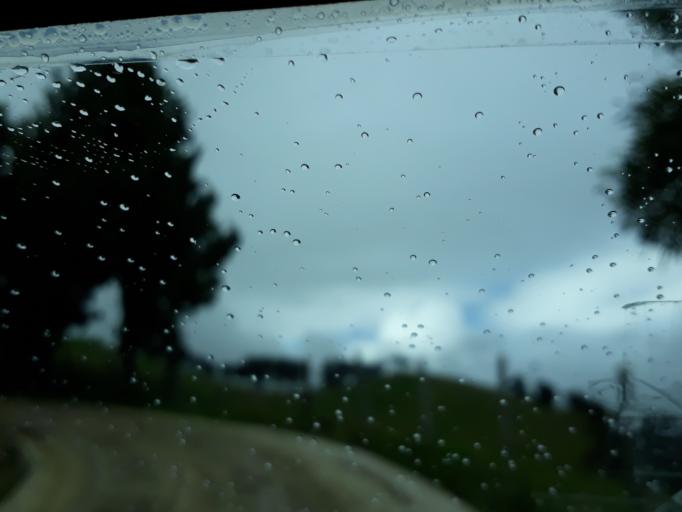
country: CO
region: Cundinamarca
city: Nemocon
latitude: 5.1525
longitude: -73.9042
